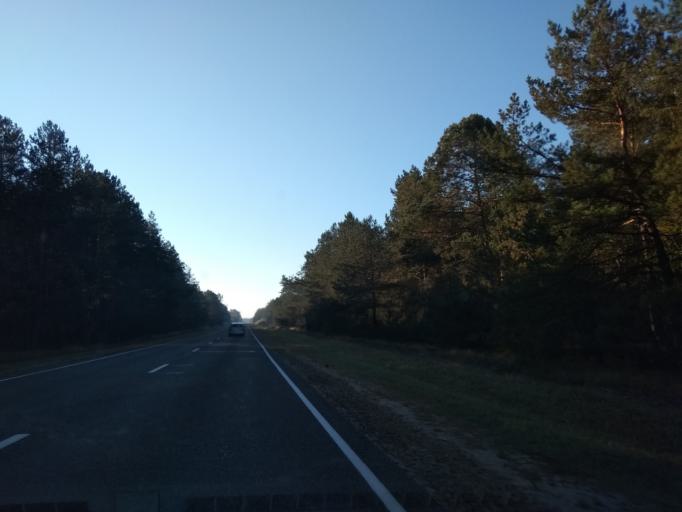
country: BY
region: Brest
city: Kobryn
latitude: 52.0848
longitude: 24.2804
